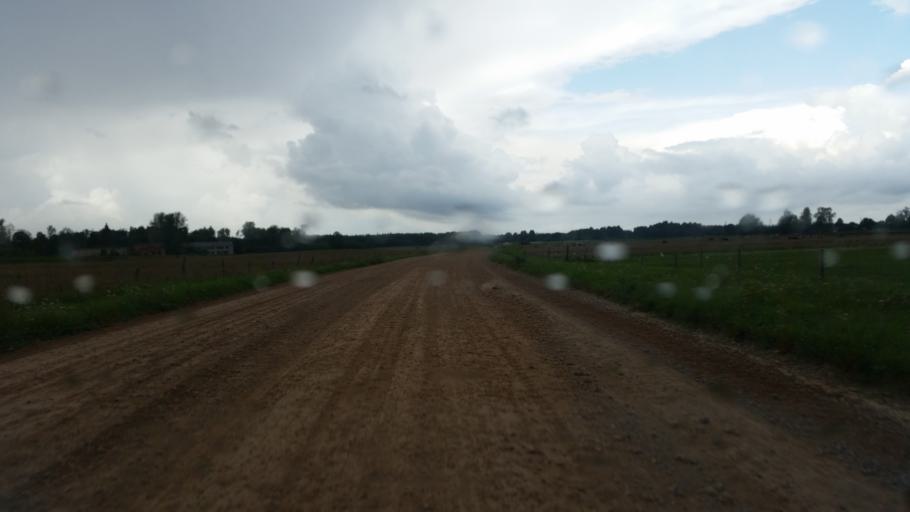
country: LV
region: Vecumnieki
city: Vecumnieki
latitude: 56.4266
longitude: 24.4692
